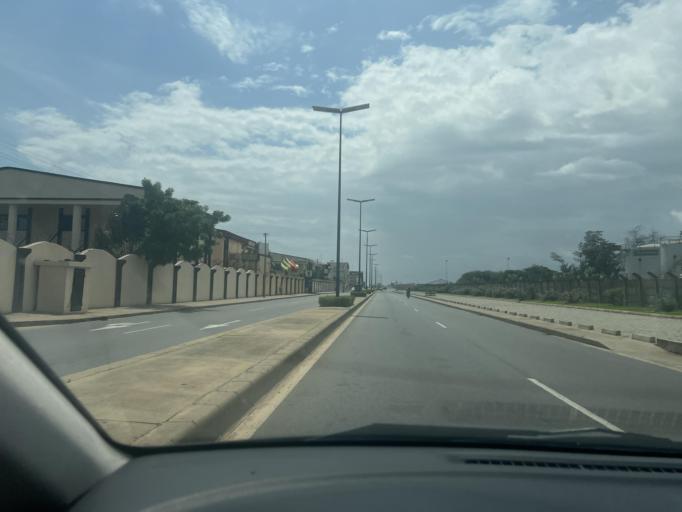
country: BJ
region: Littoral
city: Cotonou
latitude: 6.3497
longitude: 2.3842
